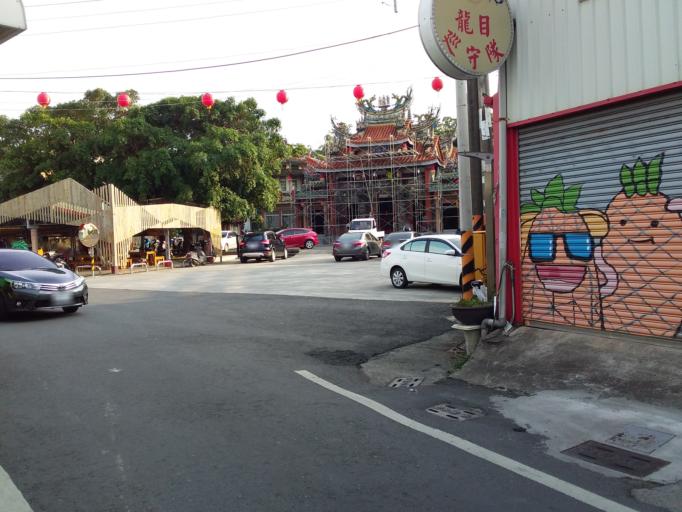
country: TW
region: Taiwan
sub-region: Pingtung
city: Pingtung
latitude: 22.6881
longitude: 120.4119
